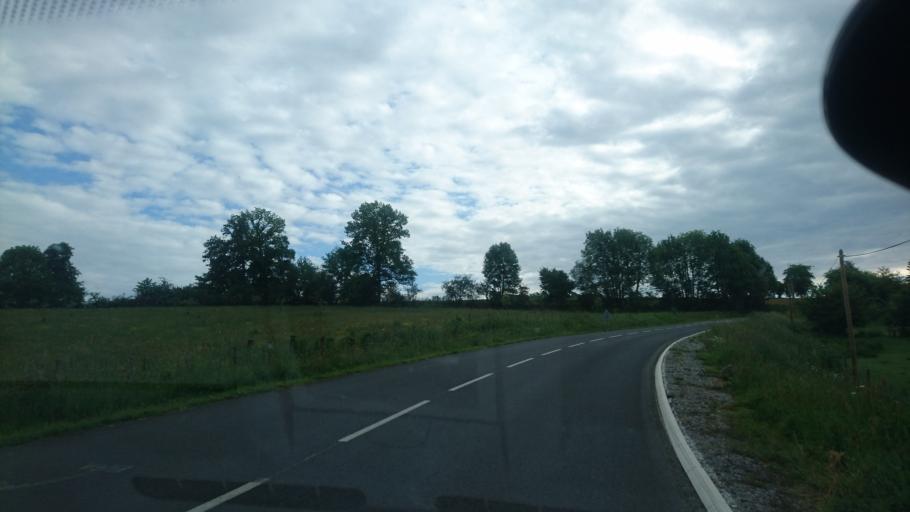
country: FR
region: Limousin
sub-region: Departement de la Haute-Vienne
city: Saint-Germain-les-Belles
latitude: 45.6252
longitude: 1.5052
